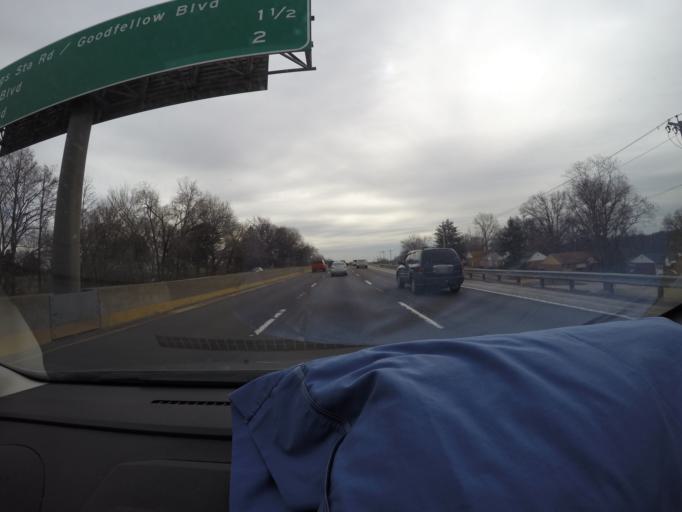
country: US
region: Missouri
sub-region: Saint Louis County
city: Northwoods
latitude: 38.7086
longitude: -90.2788
